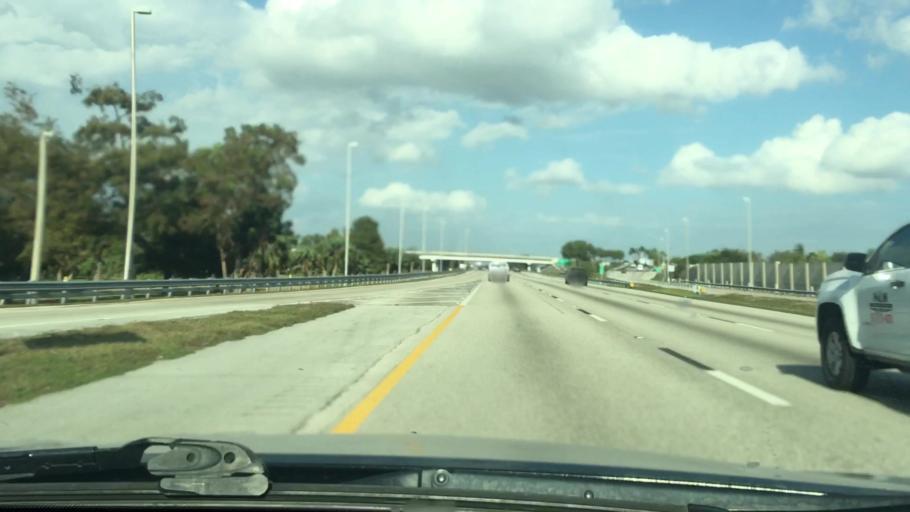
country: US
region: Florida
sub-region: Broward County
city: Coconut Creek
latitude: 26.2280
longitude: -80.1798
